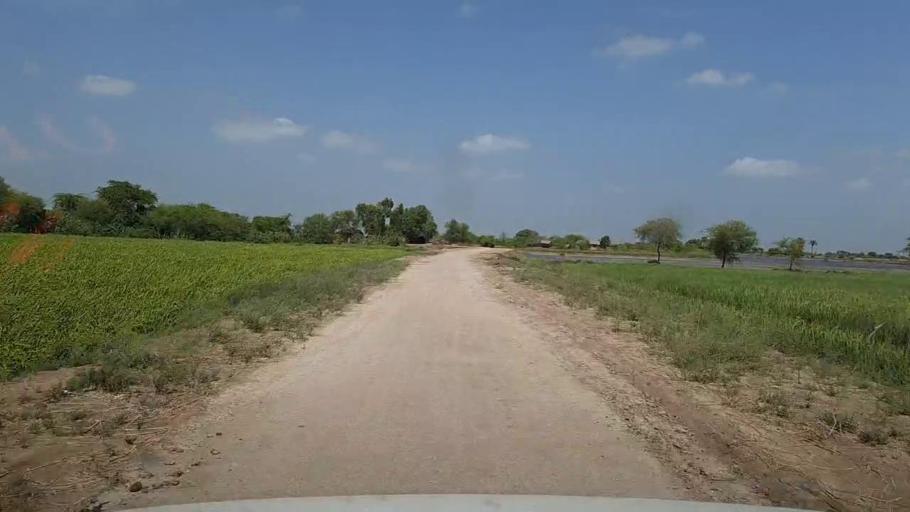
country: PK
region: Sindh
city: Kario
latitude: 24.6921
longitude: 68.5880
